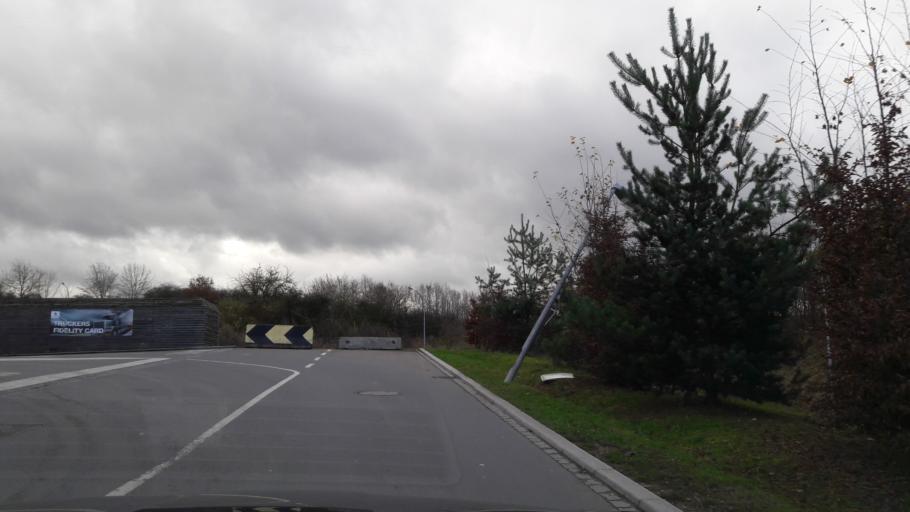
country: DE
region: Rheinland-Pfalz
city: Echternacherbruck
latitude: 49.8096
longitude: 6.4347
